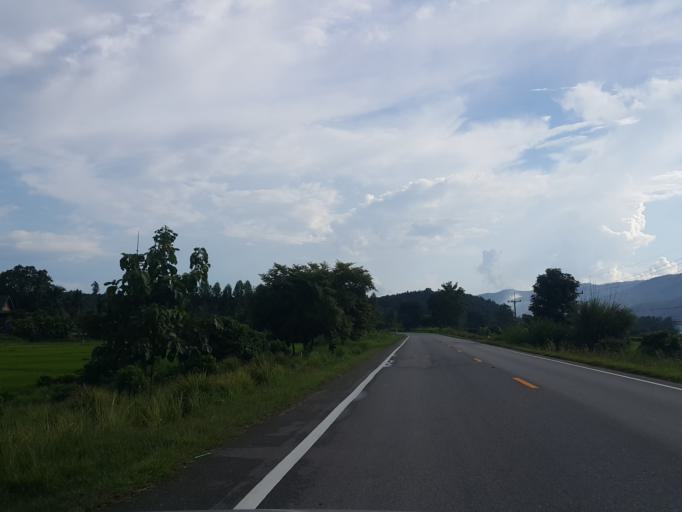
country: TH
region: Chiang Mai
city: Phrao
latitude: 19.2190
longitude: 99.1825
